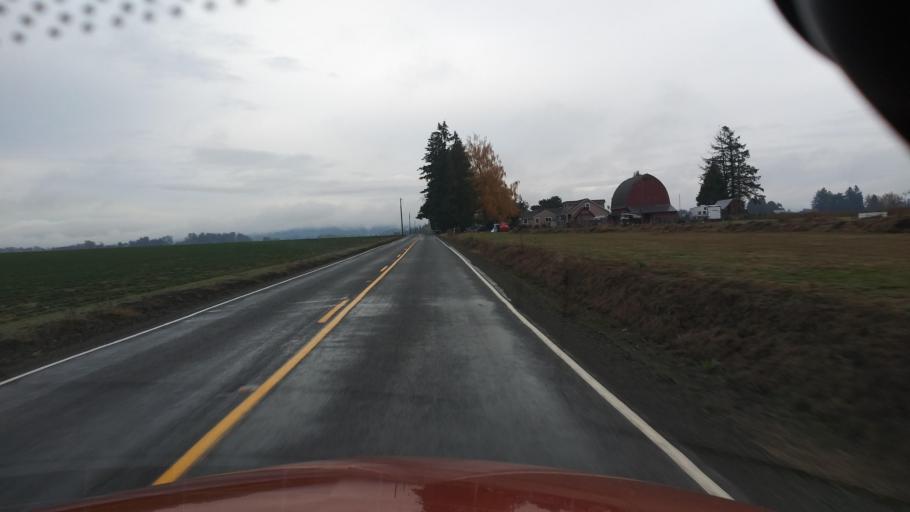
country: US
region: Oregon
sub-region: Washington County
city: North Plains
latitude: 45.5824
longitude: -123.0187
